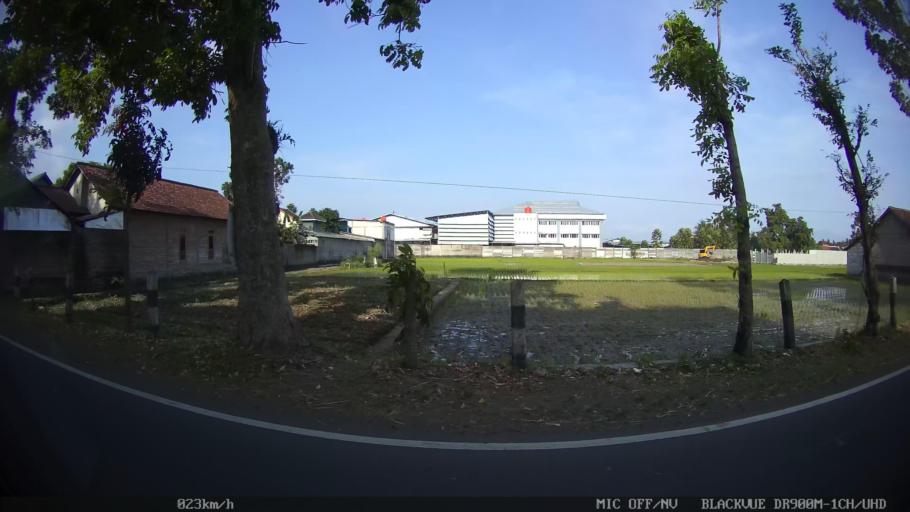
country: ID
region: Daerah Istimewa Yogyakarta
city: Bantul
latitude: -7.8771
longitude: 110.3200
